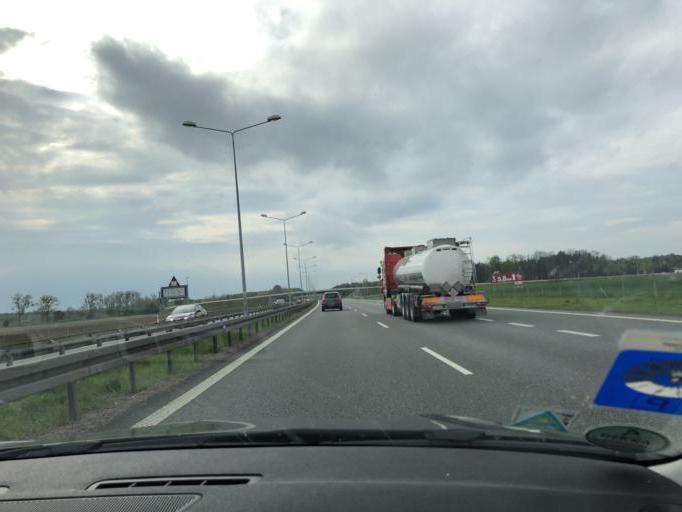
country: PL
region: Opole Voivodeship
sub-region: Powiat opolski
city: Dabrowa
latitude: 50.6593
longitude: 17.7043
